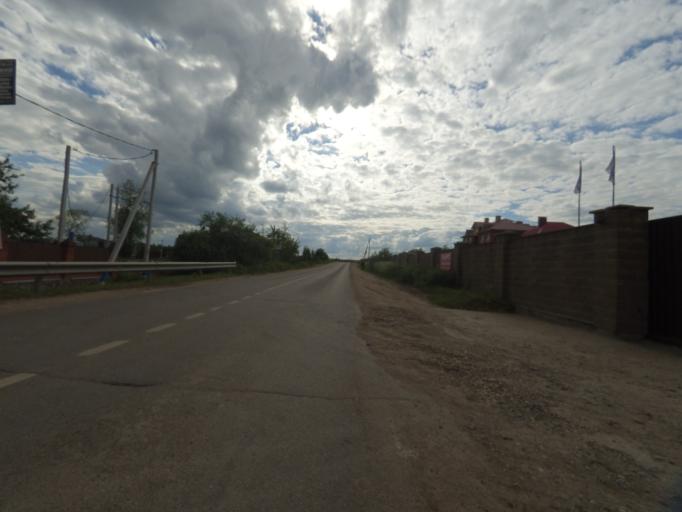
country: RU
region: Moskovskaya
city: Yermolino
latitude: 56.1244
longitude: 37.5434
